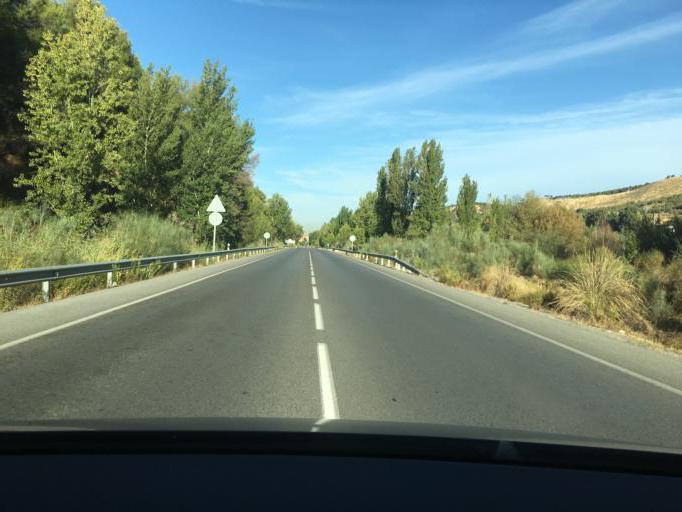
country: ES
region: Andalusia
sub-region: Provincia de Granada
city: Cenes de la Vega
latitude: 37.1579
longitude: -3.5509
